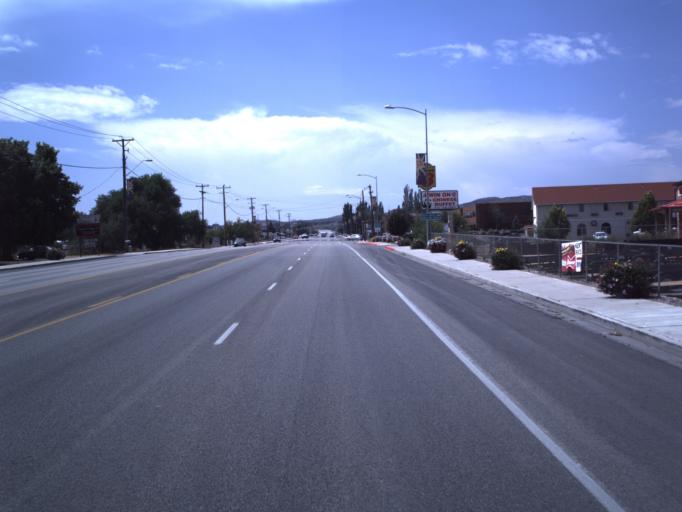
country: US
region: Utah
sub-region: Uintah County
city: Vernal
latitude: 40.4445
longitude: -109.5583
